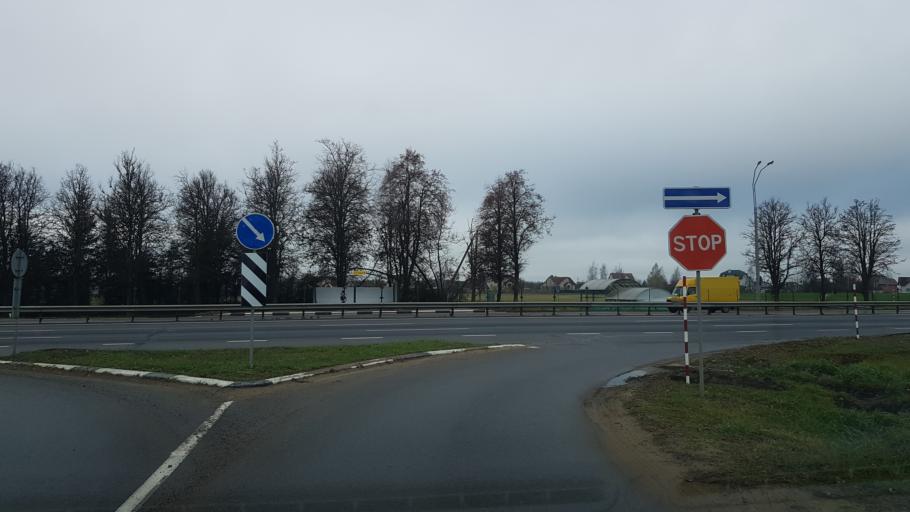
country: BY
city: Fanipol
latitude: 53.7516
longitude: 27.3264
